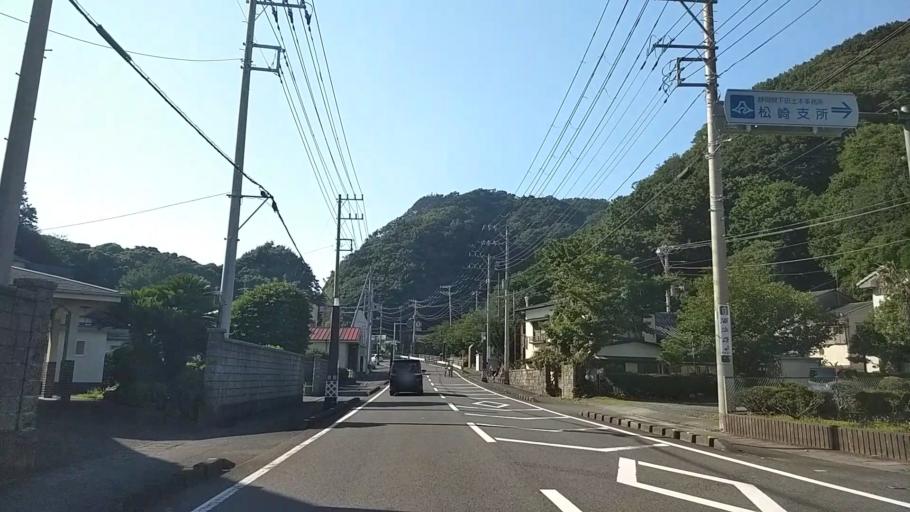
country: JP
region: Shizuoka
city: Shimoda
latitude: 34.7589
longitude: 138.7786
